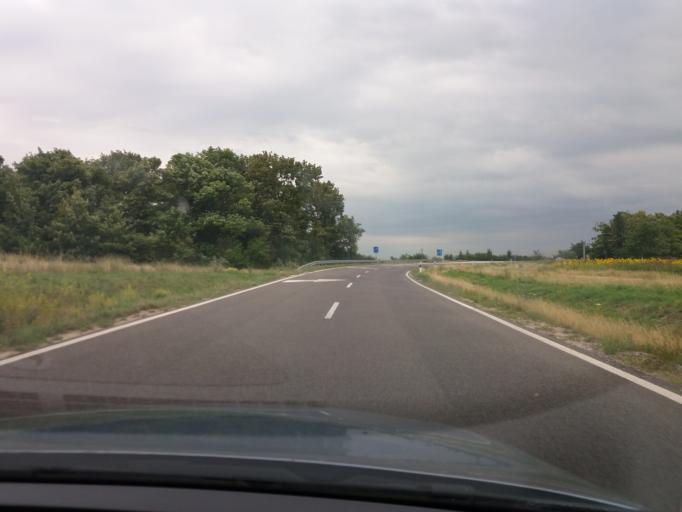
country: HU
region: Fejer
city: Kincsesbanya
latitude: 47.2149
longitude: 18.3109
